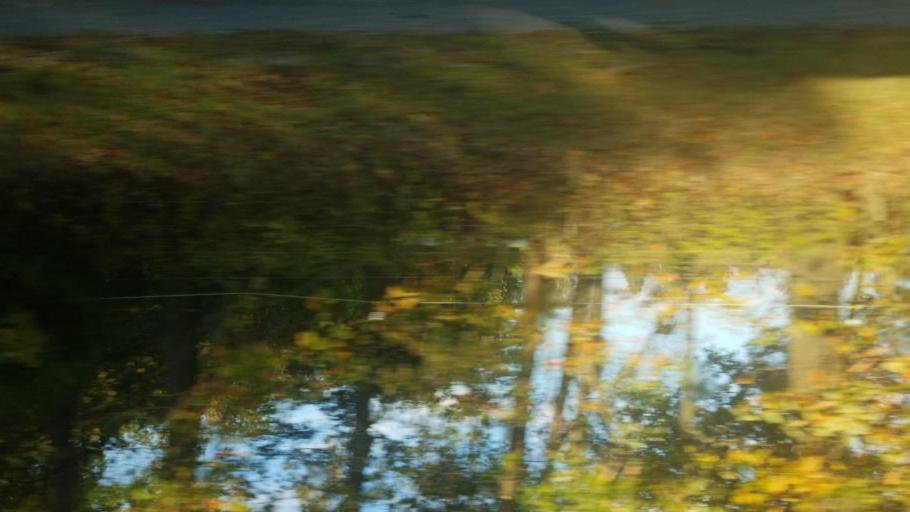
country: US
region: Illinois
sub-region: Saline County
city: Carrier Mills
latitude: 37.7981
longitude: -88.7117
